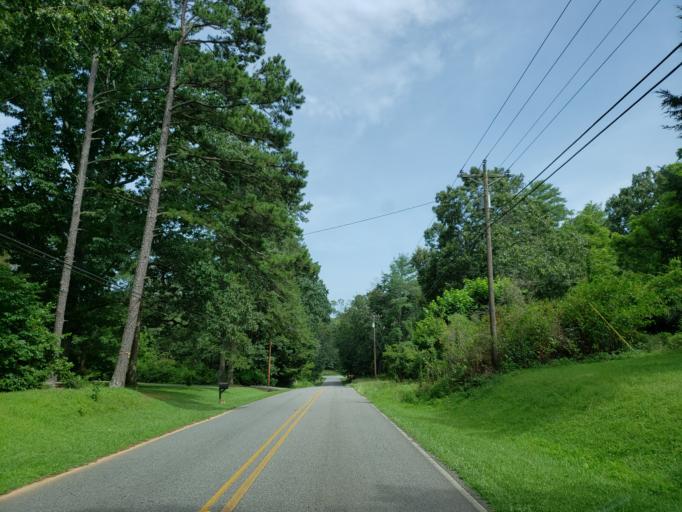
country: US
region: Georgia
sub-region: Pickens County
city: Nelson
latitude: 34.3671
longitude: -84.3774
